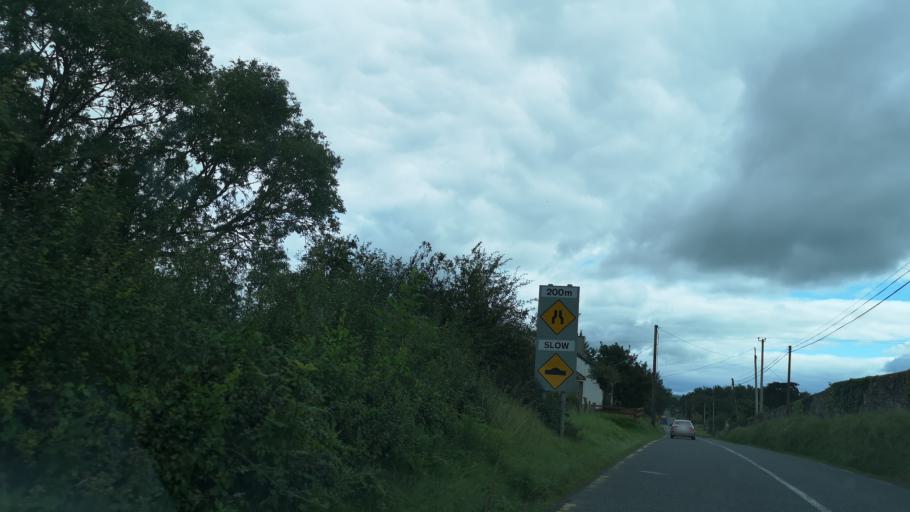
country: IE
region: Leinster
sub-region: Uibh Fhaili
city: Banagher
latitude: 53.2342
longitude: -7.9200
